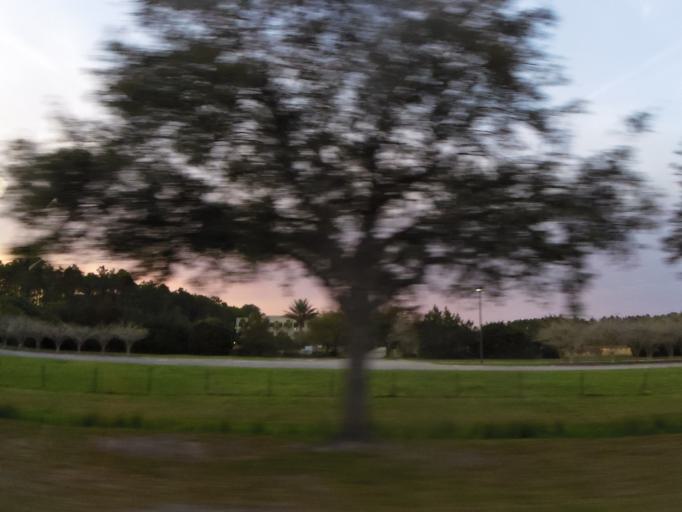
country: US
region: Florida
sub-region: Saint Johns County
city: Villano Beach
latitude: 29.9880
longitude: -81.4588
